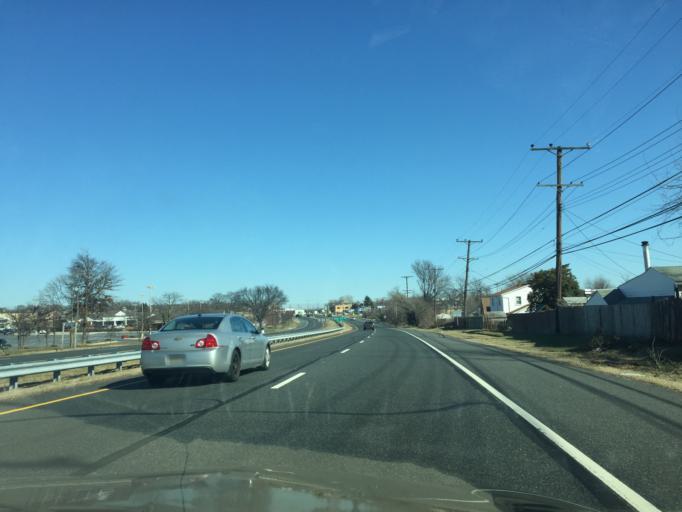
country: US
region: Maryland
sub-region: Baltimore County
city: Middle River
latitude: 39.3335
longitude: -76.4498
